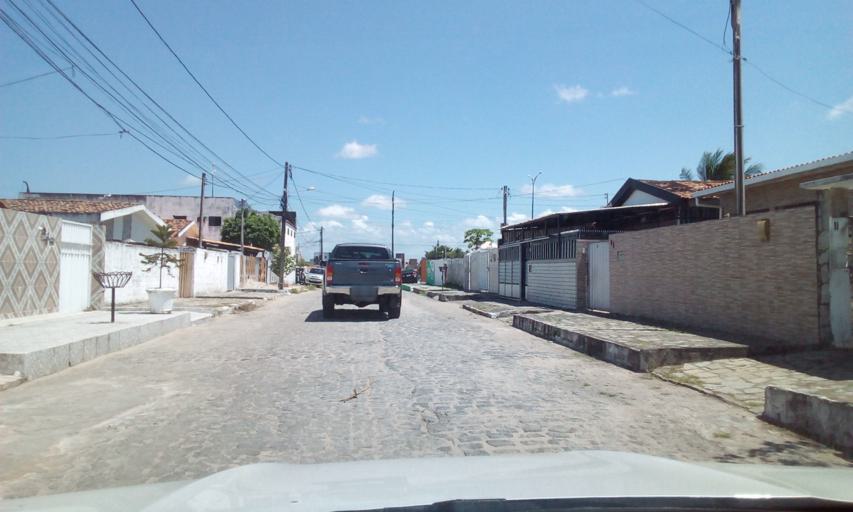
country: BR
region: Paraiba
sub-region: Joao Pessoa
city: Joao Pessoa
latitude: -7.1672
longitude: -34.8572
